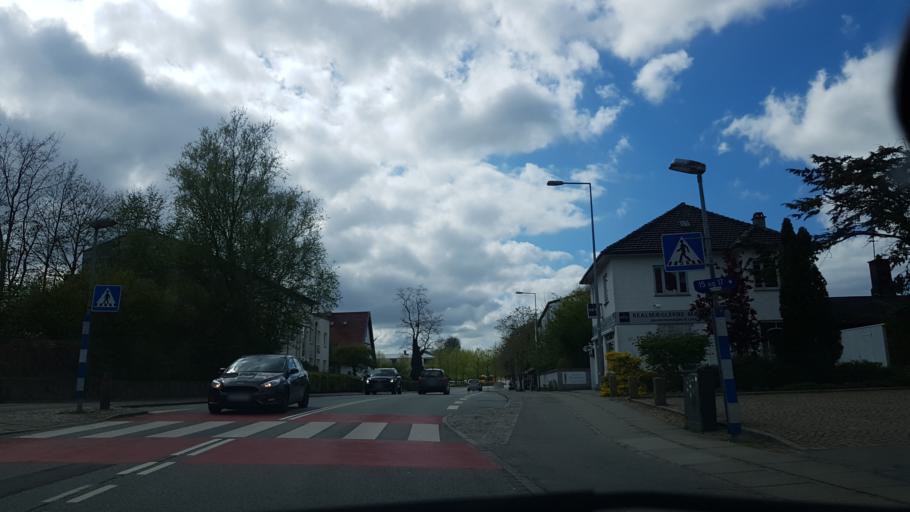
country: DK
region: Capital Region
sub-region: Horsholm Kommune
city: Horsholm
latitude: 55.8789
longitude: 12.5030
